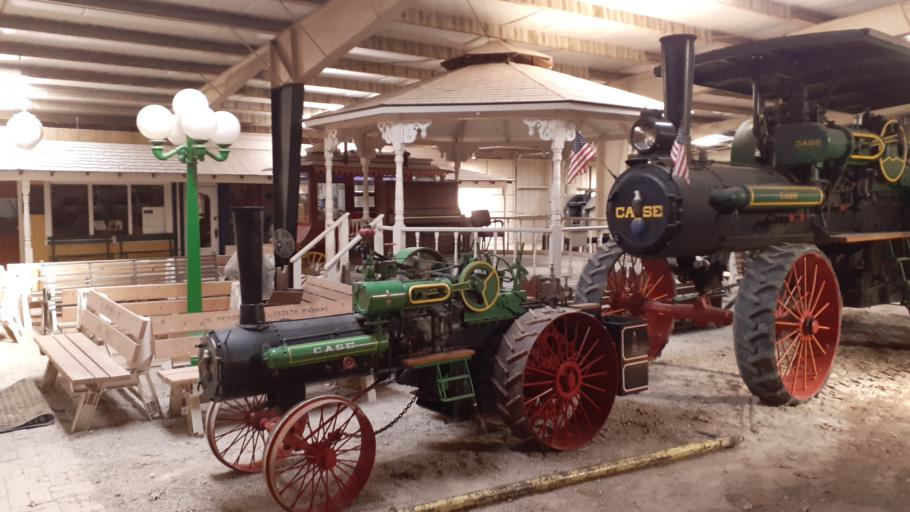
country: US
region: Iowa
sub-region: Henry County
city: Mount Pleasant
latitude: 40.9549
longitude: -91.5485
